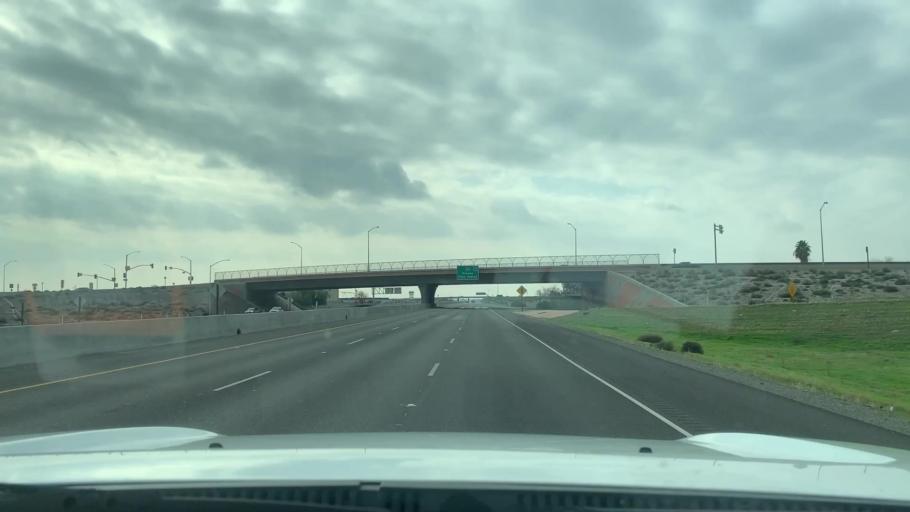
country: US
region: California
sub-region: Kings County
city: Lemoore
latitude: 36.2871
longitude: -119.7973
